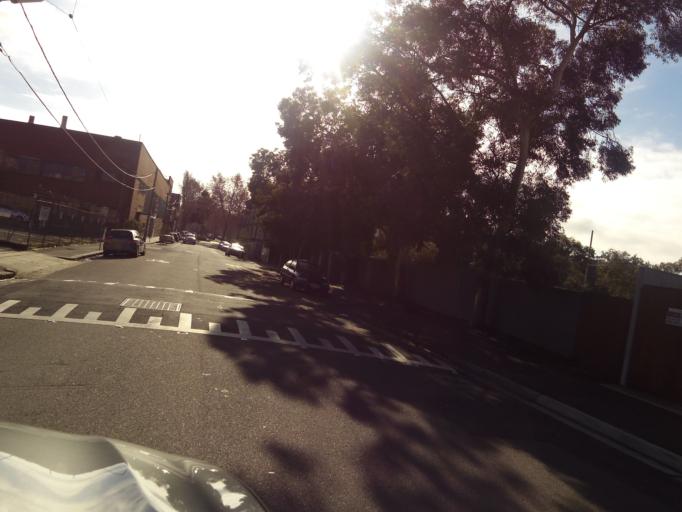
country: AU
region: Victoria
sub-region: Yarra
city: Richmond
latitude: -37.8178
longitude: 145.0132
